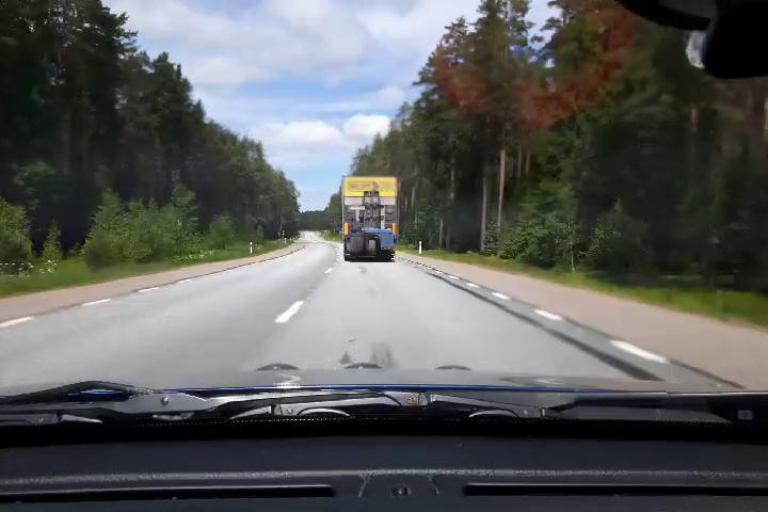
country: SE
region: Uppsala
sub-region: Tierps Kommun
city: Tierp
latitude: 60.1989
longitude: 17.4814
